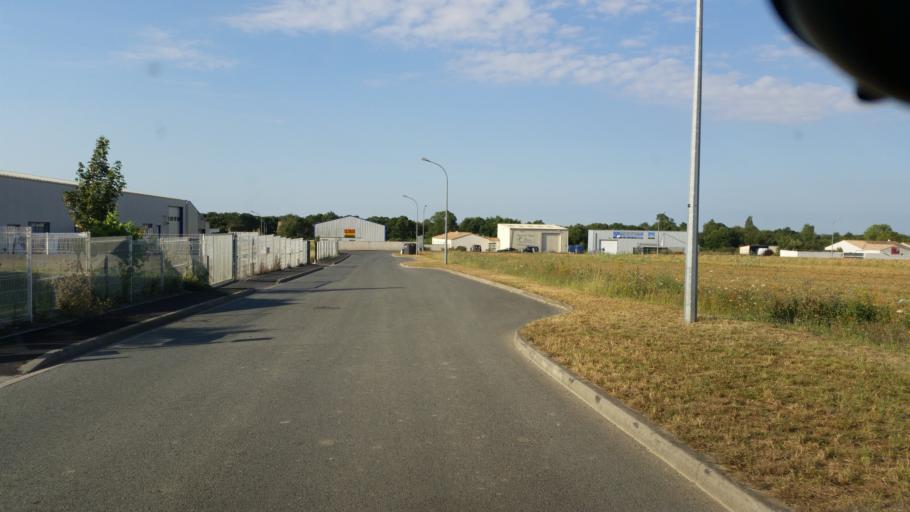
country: FR
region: Poitou-Charentes
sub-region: Departement de la Charente-Maritime
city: Saint-Jean-de-Liversay
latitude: 46.2316
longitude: -0.8847
